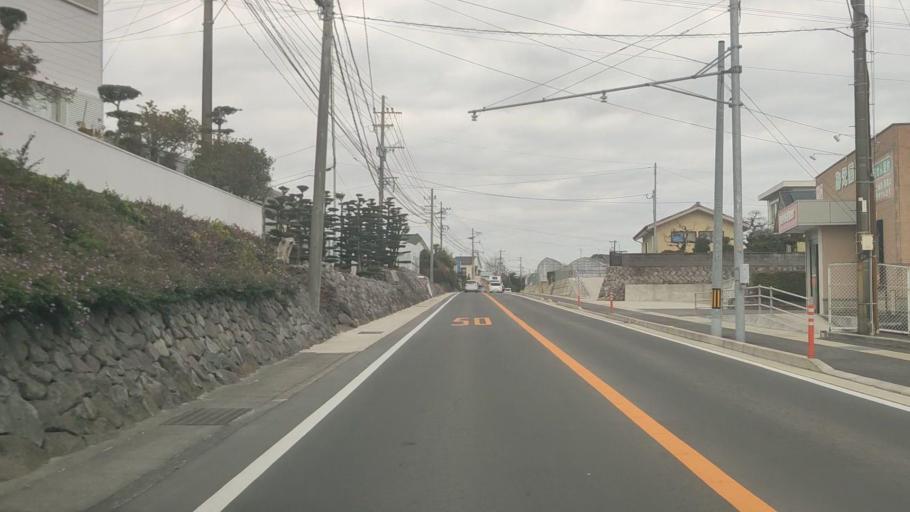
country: JP
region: Nagasaki
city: Shimabara
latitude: 32.8158
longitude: 130.3561
